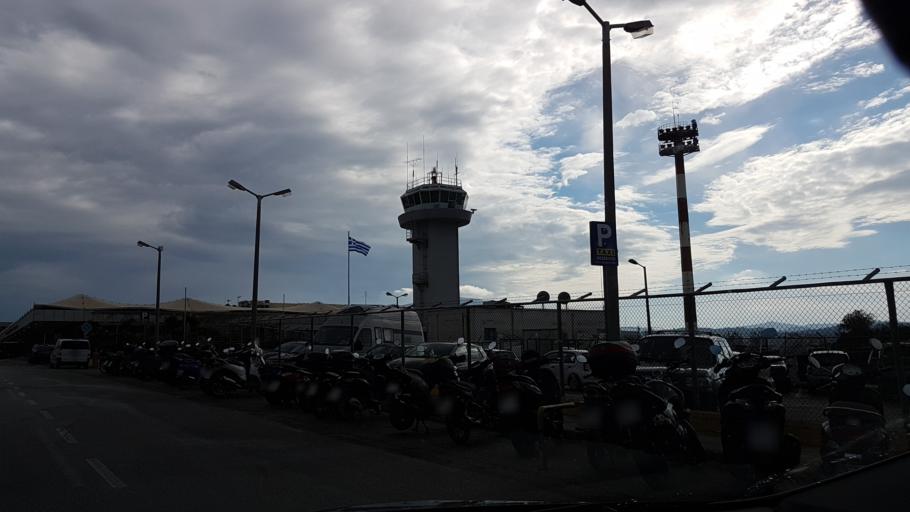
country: GR
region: Ionian Islands
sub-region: Nomos Kerkyras
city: Kerkyra
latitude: 39.6089
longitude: 19.9145
